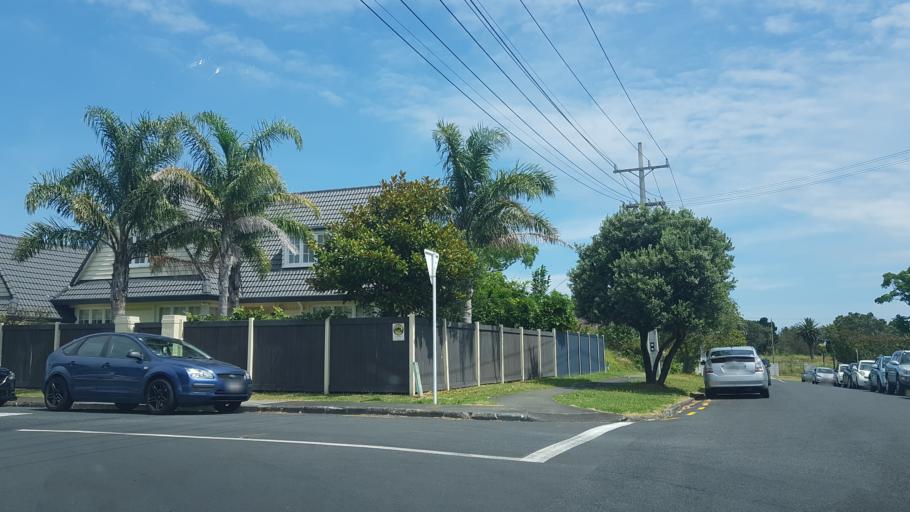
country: NZ
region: Auckland
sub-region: Auckland
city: North Shore
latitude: -36.7860
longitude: 174.7606
